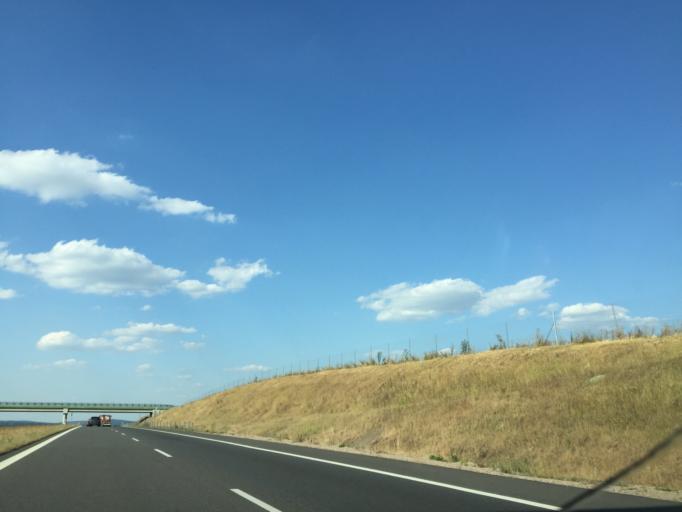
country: PL
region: Swietokrzyskie
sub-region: Powiat jedrzejowski
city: Sobkow
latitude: 50.7147
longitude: 20.4078
